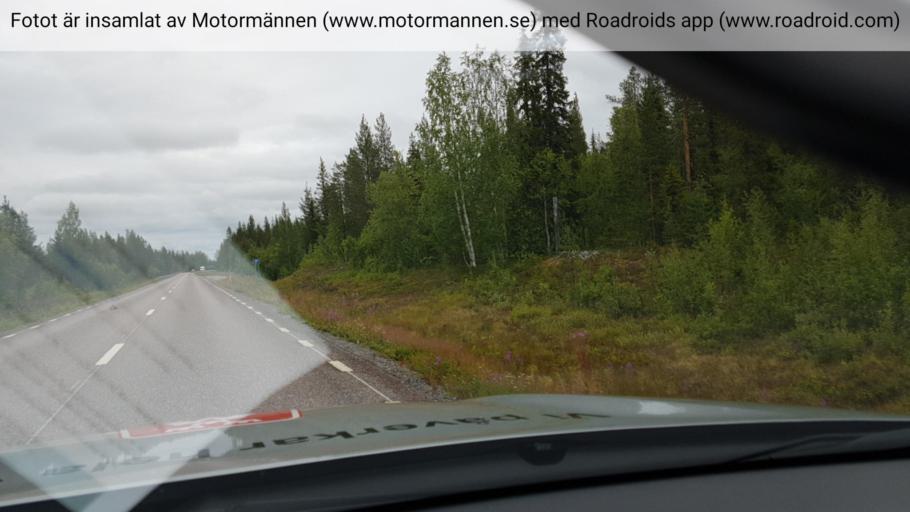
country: SE
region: Norrbotten
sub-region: Gallivare Kommun
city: Gaellivare
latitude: 67.0707
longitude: 21.5352
